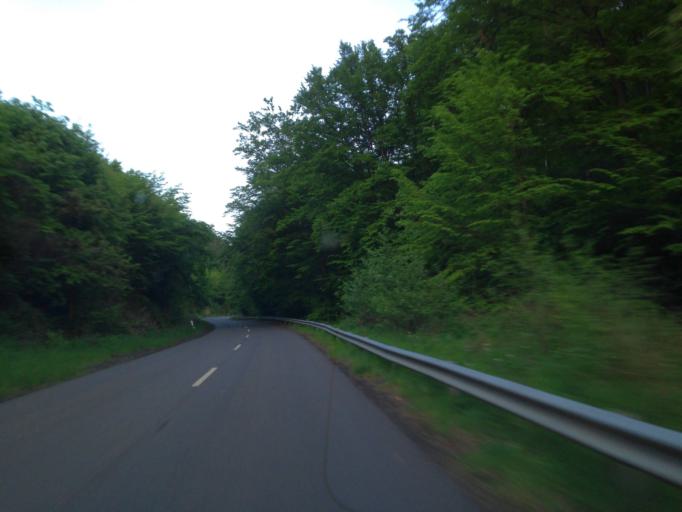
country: HU
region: Nograd
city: Batonyterenye
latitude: 47.8967
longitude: 19.8252
